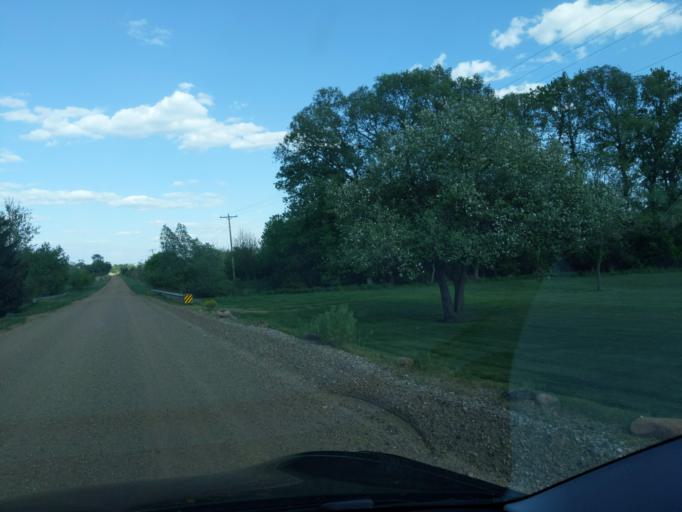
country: US
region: Michigan
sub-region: Eaton County
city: Potterville
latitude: 42.6829
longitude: -84.7371
